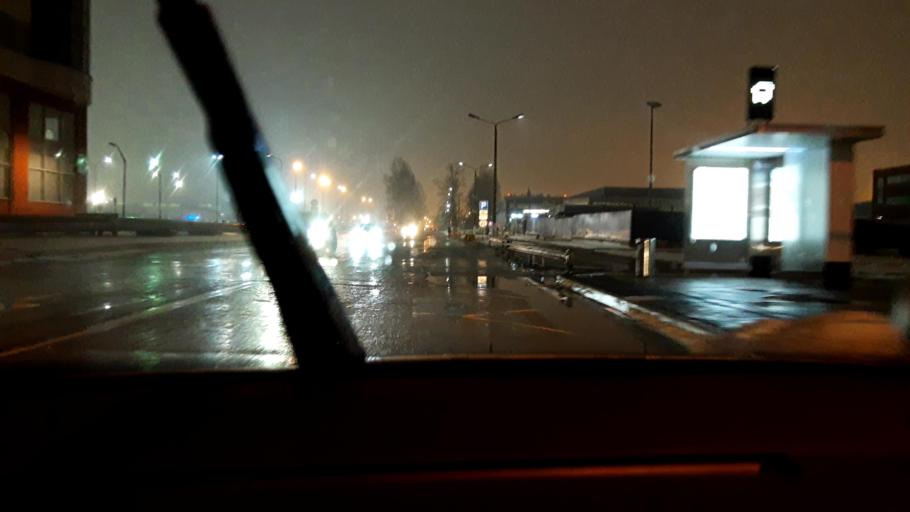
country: RU
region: Moskovskaya
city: Yakovlevskoye
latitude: 55.4182
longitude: 37.8889
